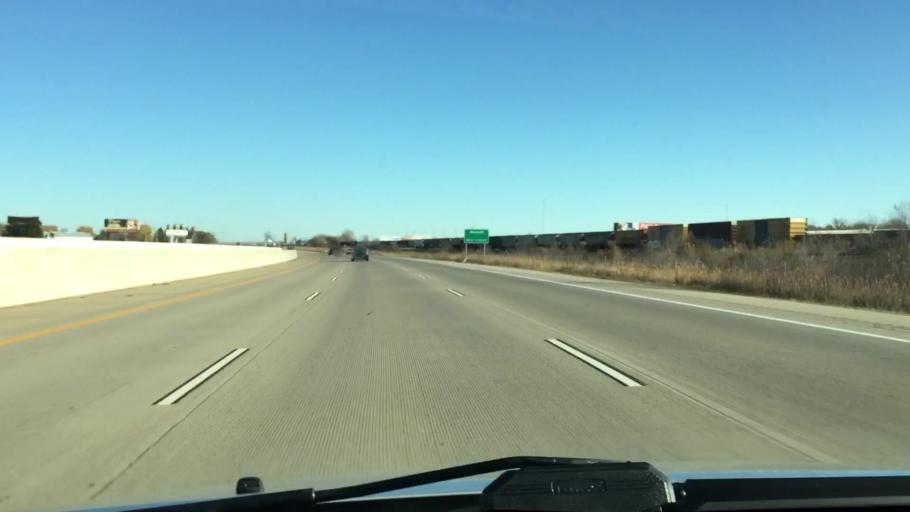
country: US
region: Wisconsin
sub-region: Winnebago County
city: Neenah
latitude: 44.1262
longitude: -88.4993
